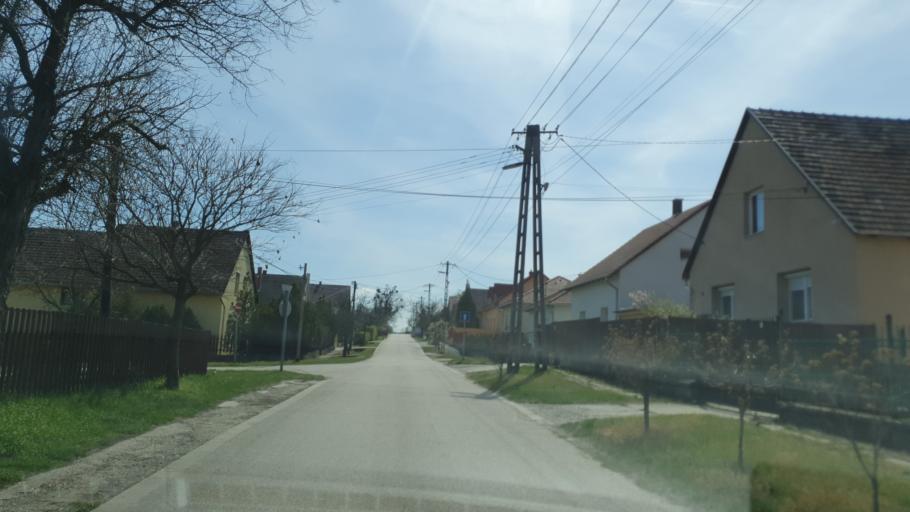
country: HU
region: Komarom-Esztergom
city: Oroszlany
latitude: 47.4860
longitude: 18.3062
